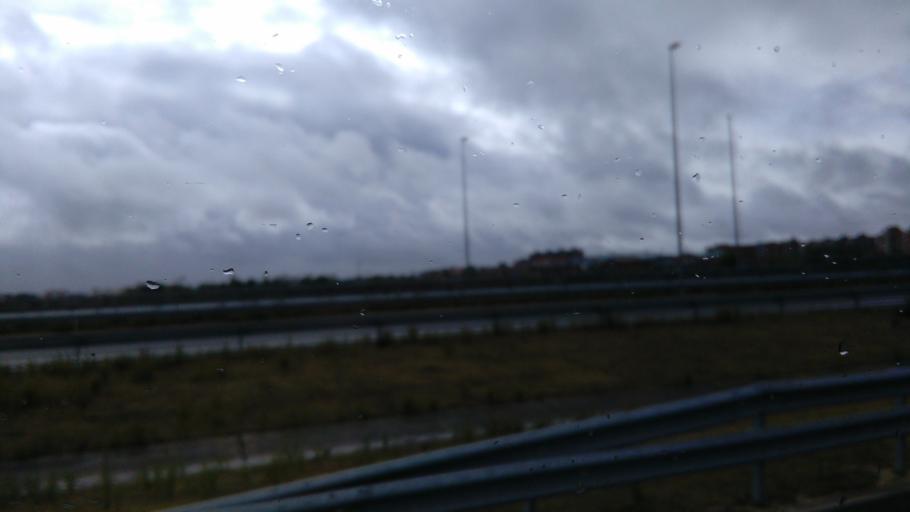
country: ES
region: Madrid
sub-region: Provincia de Madrid
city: Mostoles
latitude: 40.3086
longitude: -3.8322
